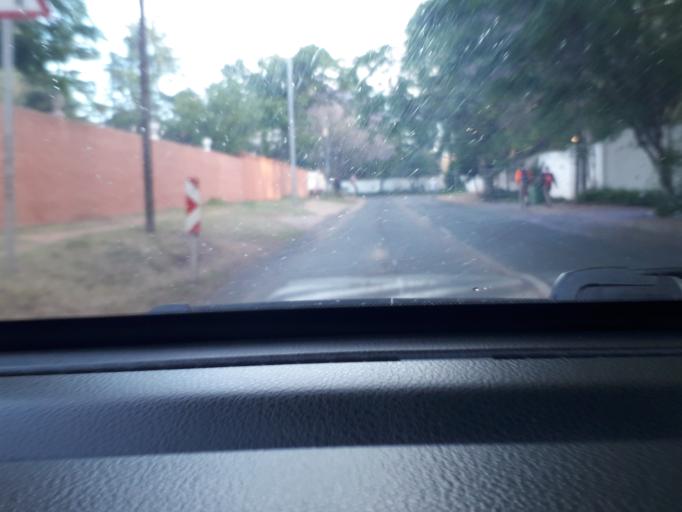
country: ZA
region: Gauteng
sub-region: City of Johannesburg Metropolitan Municipality
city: Johannesburg
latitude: -26.1115
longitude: 28.0636
